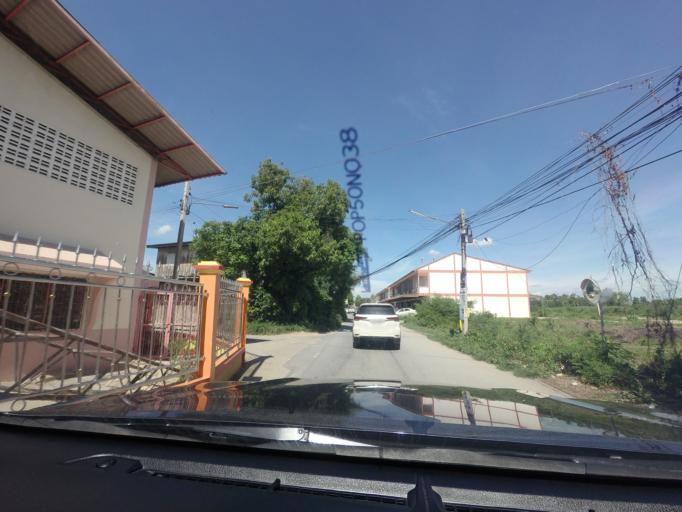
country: TH
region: Suphan Buri
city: Song Phi Nong
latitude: 14.1779
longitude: 99.9365
